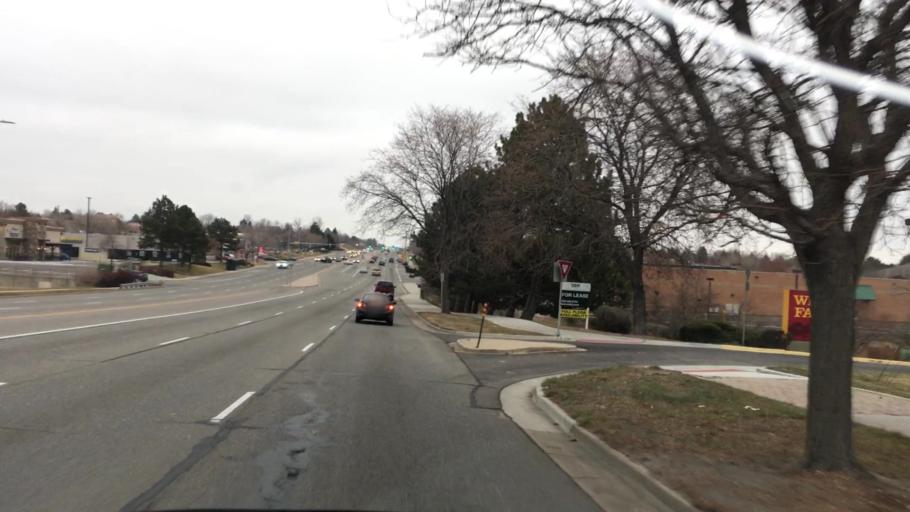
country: US
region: Colorado
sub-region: Jefferson County
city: Arvada
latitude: 39.8391
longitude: -105.0817
